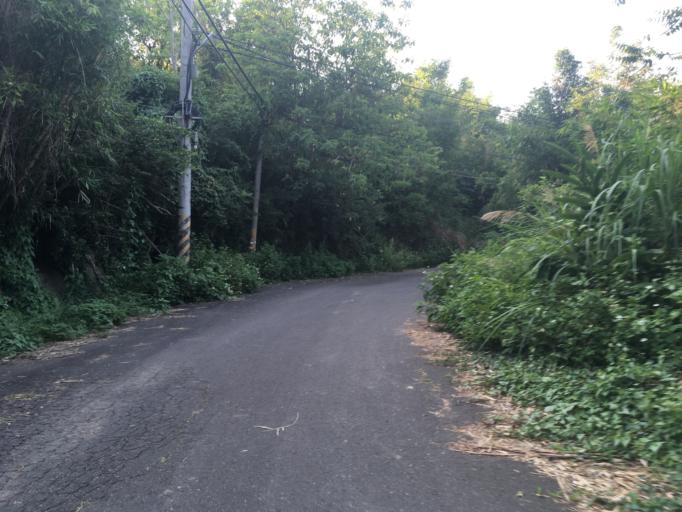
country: TW
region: Taiwan
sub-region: Hsinchu
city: Hsinchu
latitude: 24.7387
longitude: 120.9878
